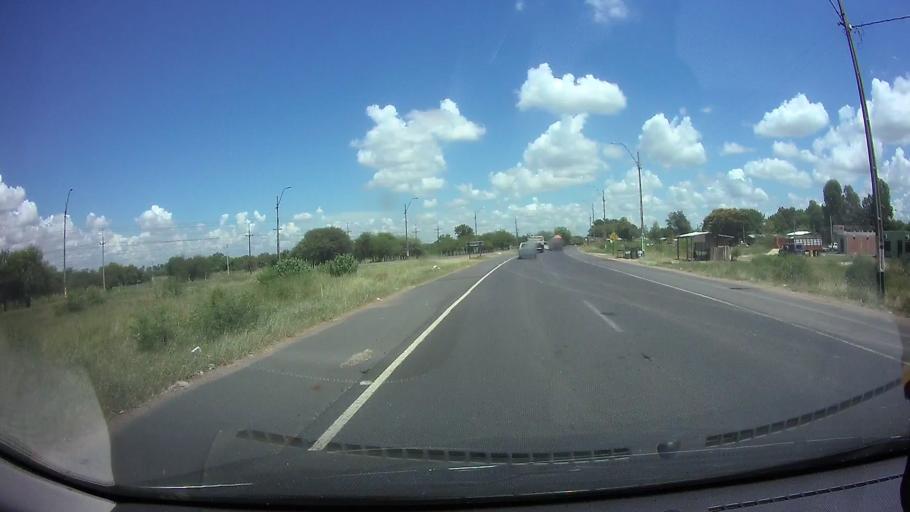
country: PY
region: Central
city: Colonia Mariano Roque Alonso
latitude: -25.1712
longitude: -57.5662
